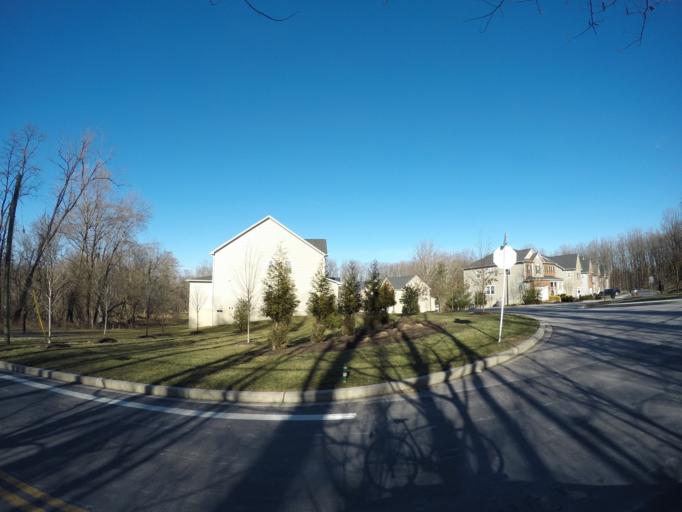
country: US
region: Maryland
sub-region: Howard County
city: Ellicott City
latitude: 39.2619
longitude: -76.7948
